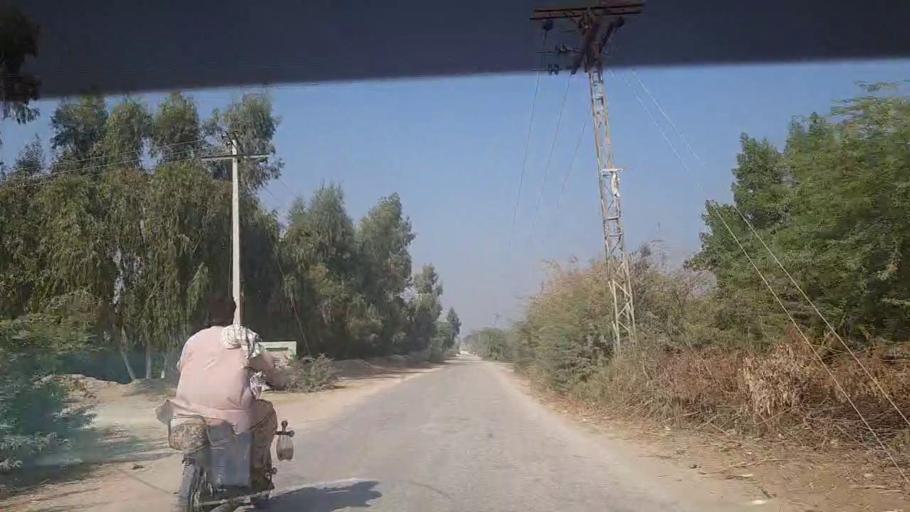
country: PK
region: Sindh
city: Kot Diji
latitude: 27.3541
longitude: 68.7112
